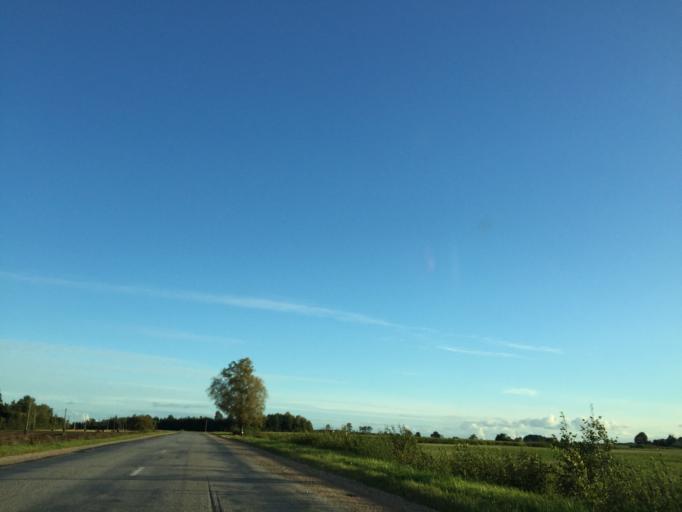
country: LV
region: Saldus Rajons
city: Saldus
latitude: 56.7368
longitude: 22.3773
